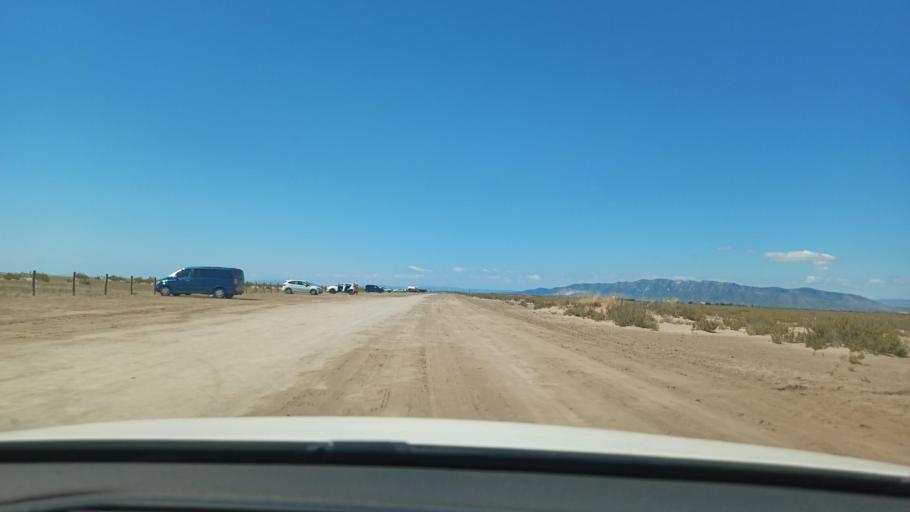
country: ES
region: Catalonia
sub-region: Provincia de Tarragona
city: Deltebre
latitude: 40.6507
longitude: 0.7759
